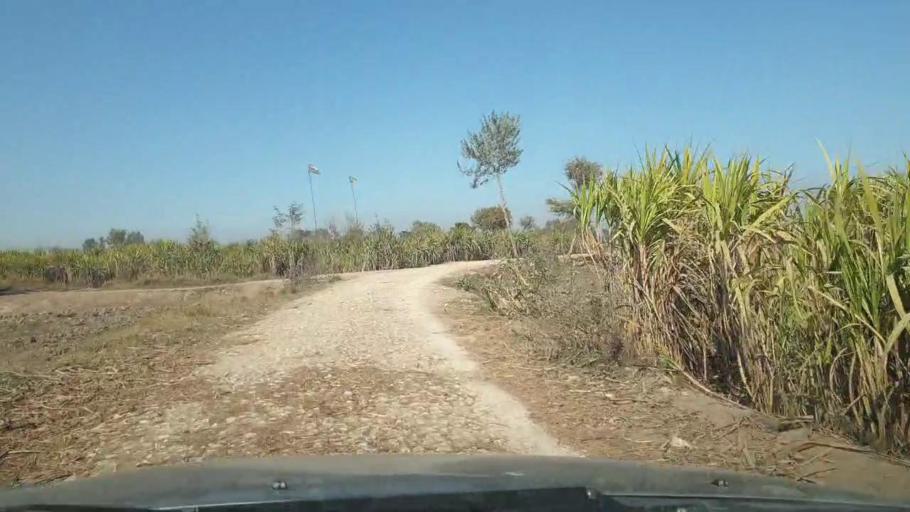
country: PK
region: Sindh
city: Ghotki
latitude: 28.0305
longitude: 69.2484
